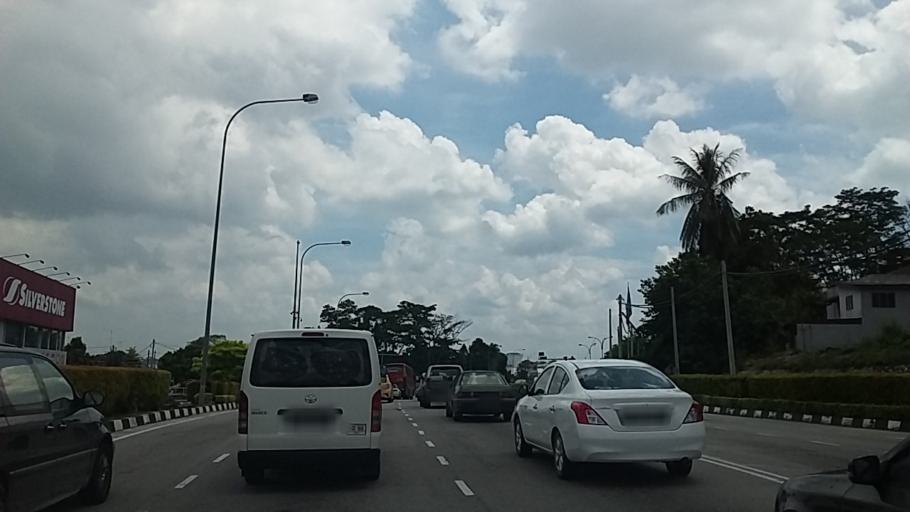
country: MY
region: Johor
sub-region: Daerah Batu Pahat
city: Batu Pahat
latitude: 1.8386
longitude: 102.9455
